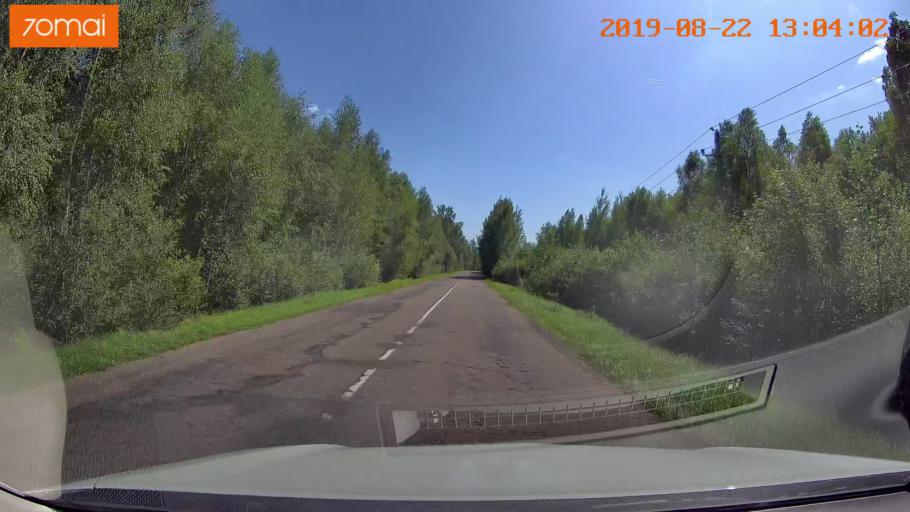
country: BY
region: Minsk
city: Prawdzinski
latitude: 53.3747
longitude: 27.8224
